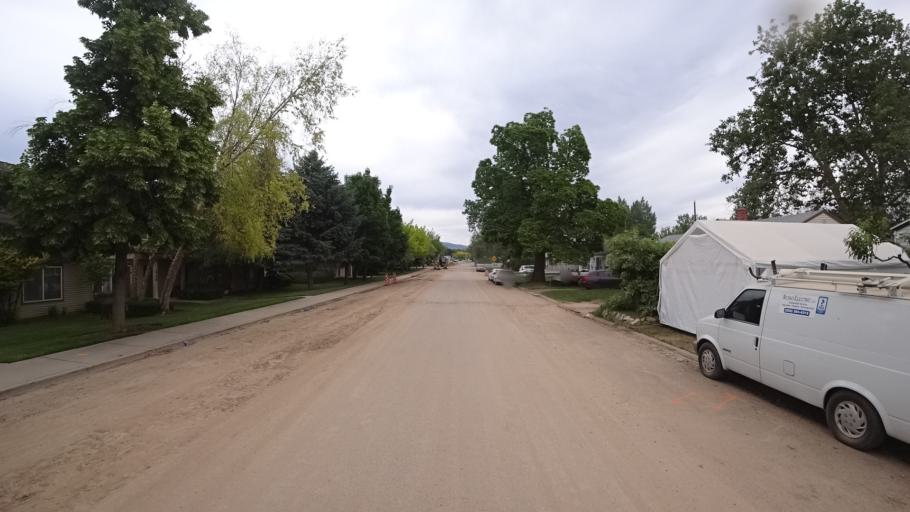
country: US
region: Idaho
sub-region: Ada County
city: Boise
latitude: 43.5808
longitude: -116.2164
